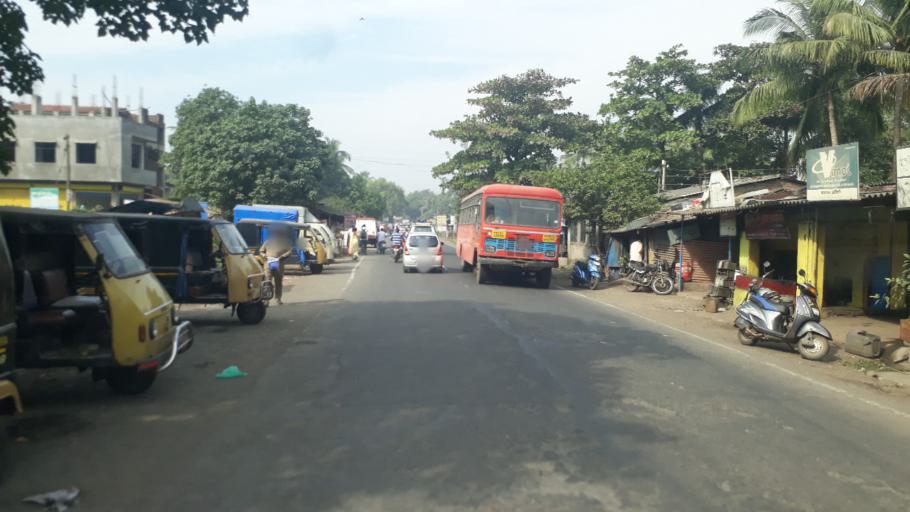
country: IN
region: Maharashtra
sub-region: Raigarh
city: Pen
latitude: 18.6874
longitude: 72.9926
